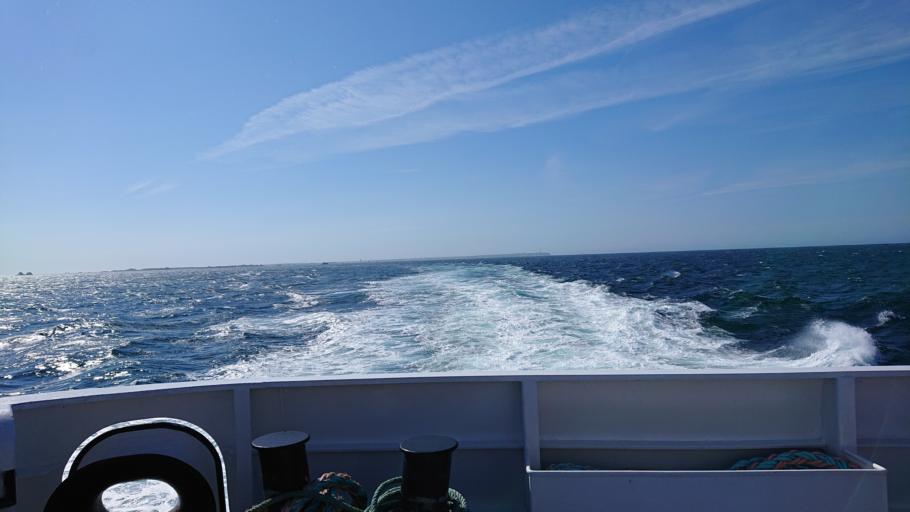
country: FR
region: Brittany
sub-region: Departement du Finistere
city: Le Conquet
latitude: 48.4131
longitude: -4.9365
